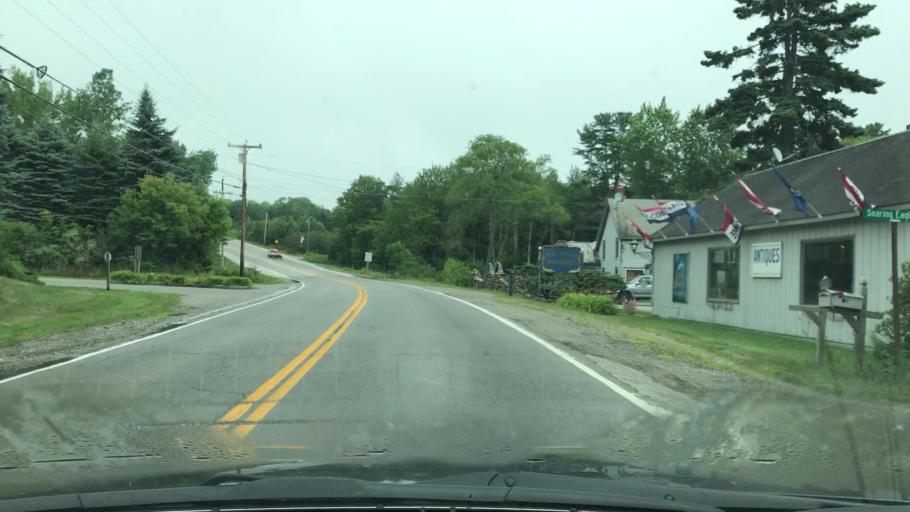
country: US
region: Maine
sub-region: Waldo County
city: Lincolnville
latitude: 44.3023
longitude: -68.9816
